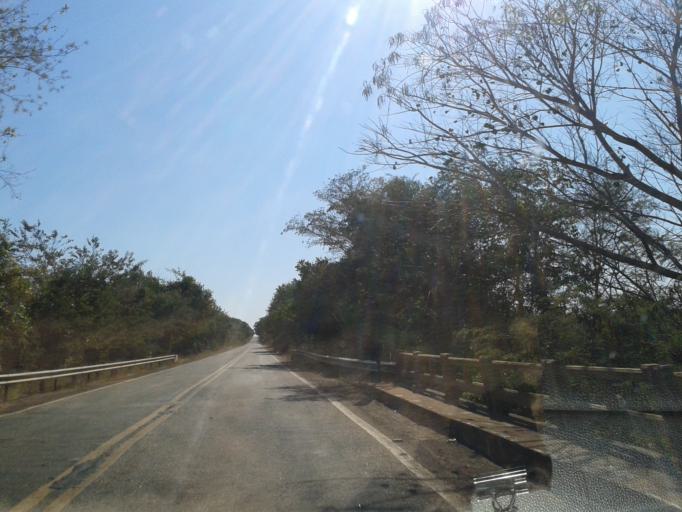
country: BR
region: Goias
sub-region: Mozarlandia
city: Mozarlandia
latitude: -14.4893
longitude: -50.4813
